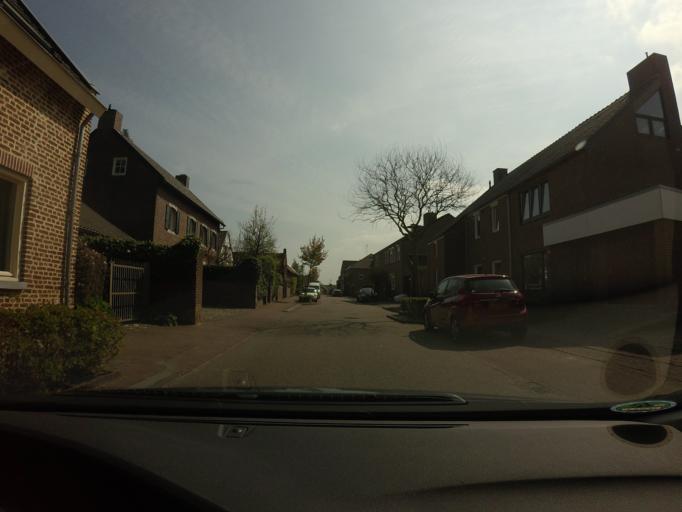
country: NL
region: Limburg
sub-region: Valkenburg aan de Geul
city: Berg
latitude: 50.8285
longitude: 5.7689
